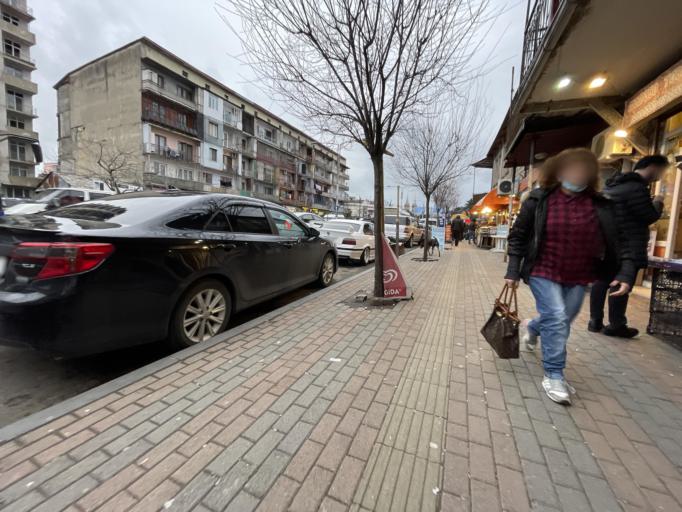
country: GE
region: Ajaria
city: Batumi
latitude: 41.6459
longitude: 41.6427
